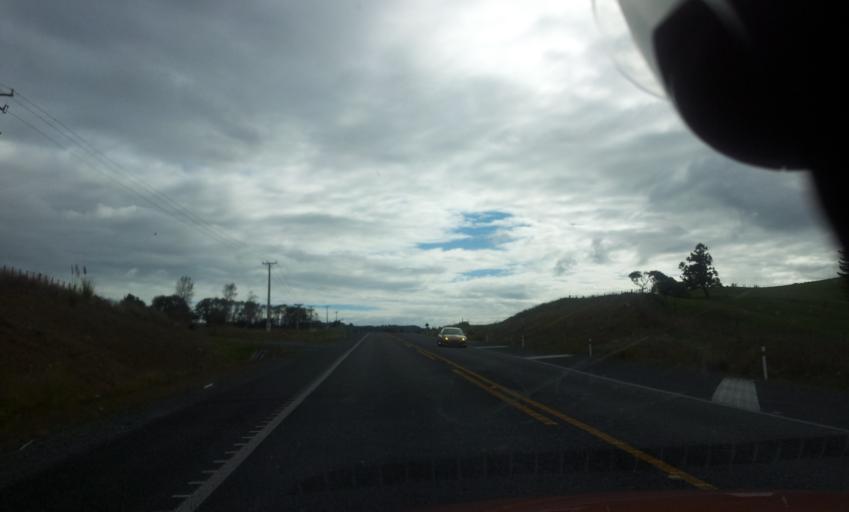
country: NZ
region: Auckland
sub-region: Auckland
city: Wellsford
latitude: -36.2446
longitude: 174.5089
